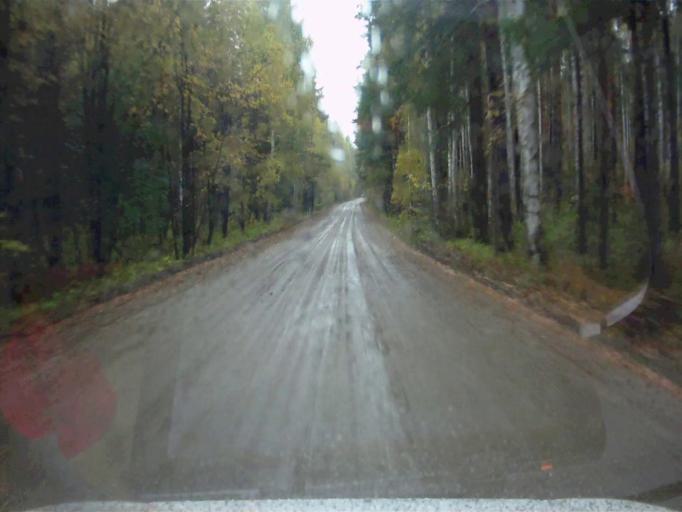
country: RU
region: Chelyabinsk
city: Kyshtym
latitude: 55.8882
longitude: 60.4649
